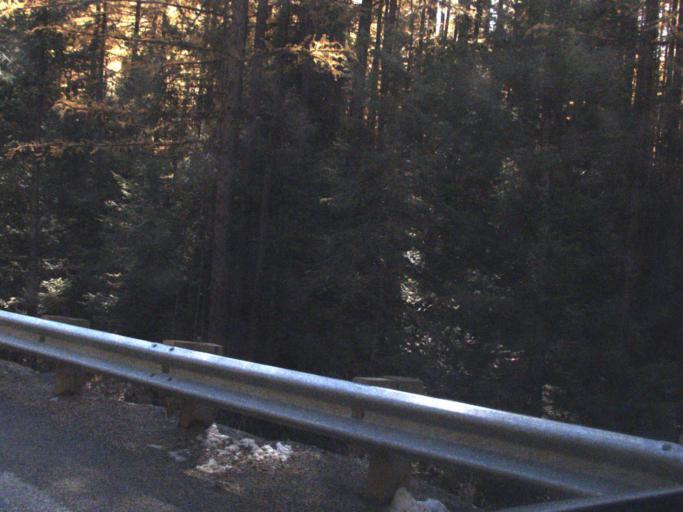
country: US
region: Washington
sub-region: Ferry County
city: Republic
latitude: 48.6272
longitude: -118.4395
